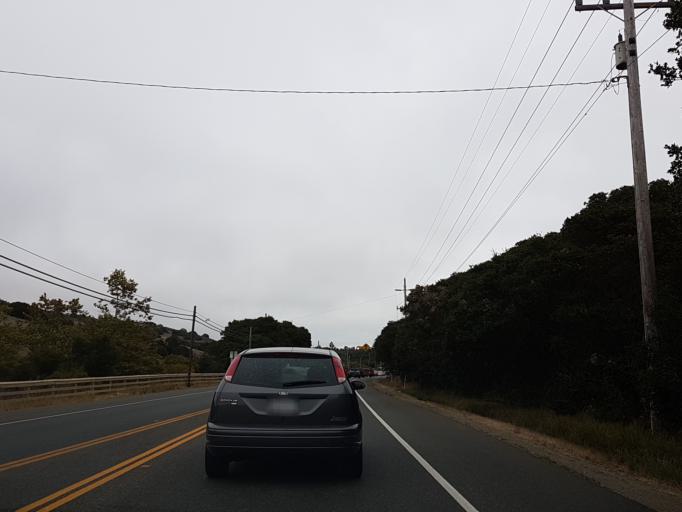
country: US
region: California
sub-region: Monterey County
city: Carmel Valley Village
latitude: 36.5703
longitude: -121.7607
